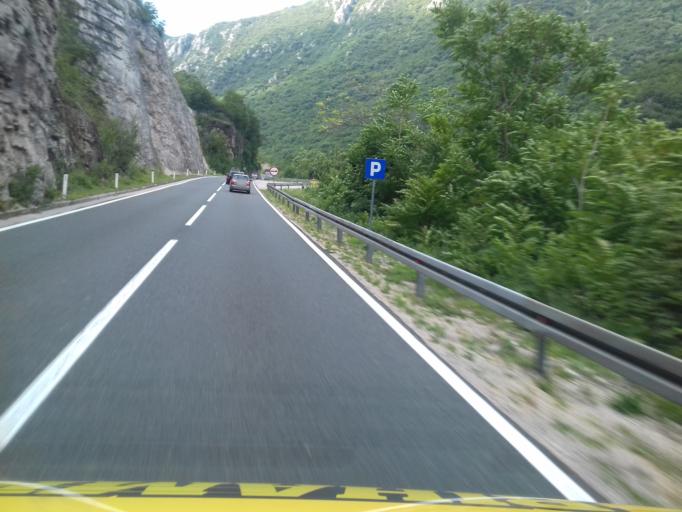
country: BA
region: Federation of Bosnia and Herzegovina
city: Jablanica
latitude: 43.5618
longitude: 17.7200
